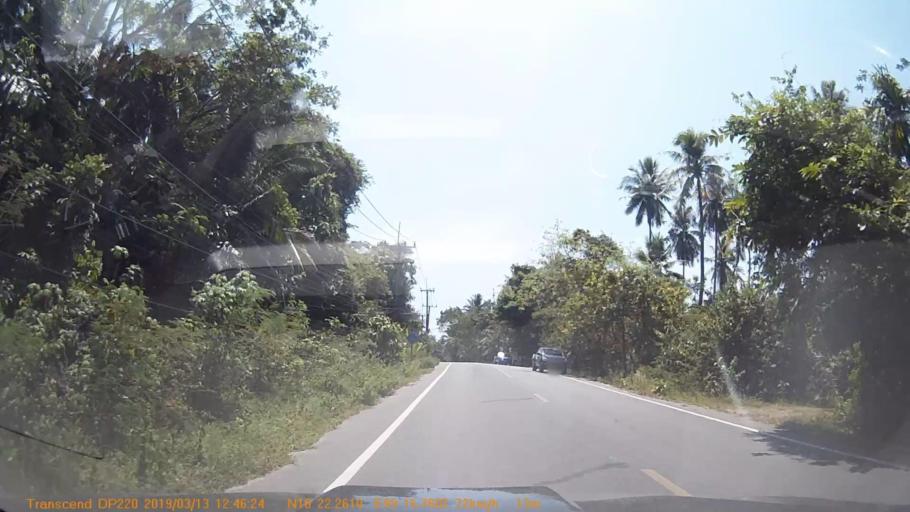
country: TH
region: Chumphon
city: Chumphon
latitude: 10.3707
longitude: 99.2626
